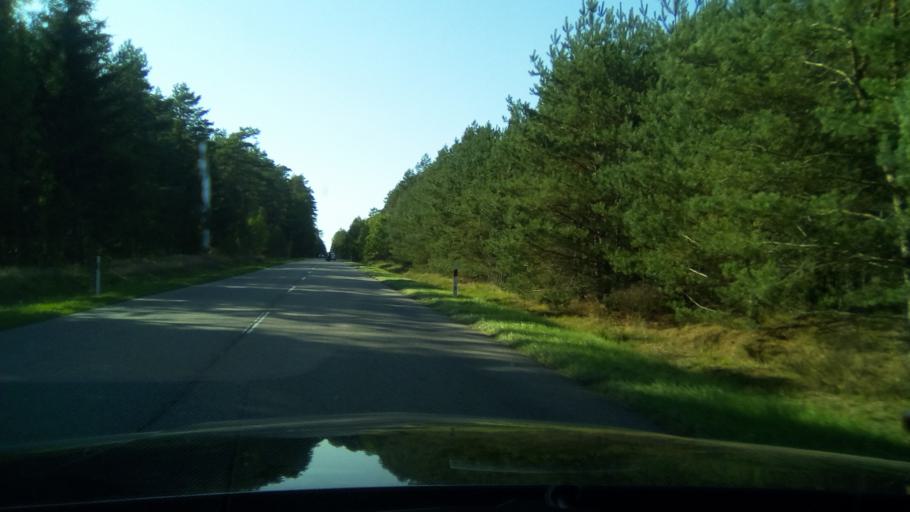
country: PL
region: West Pomeranian Voivodeship
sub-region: Powiat kamienski
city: Golczewo
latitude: 53.8123
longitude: 15.1027
